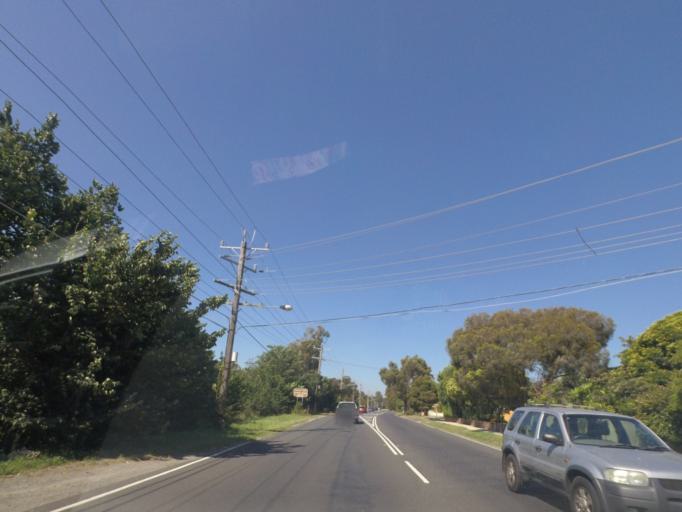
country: AU
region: Victoria
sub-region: Manningham
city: Bulleen
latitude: -37.7575
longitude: 145.0876
